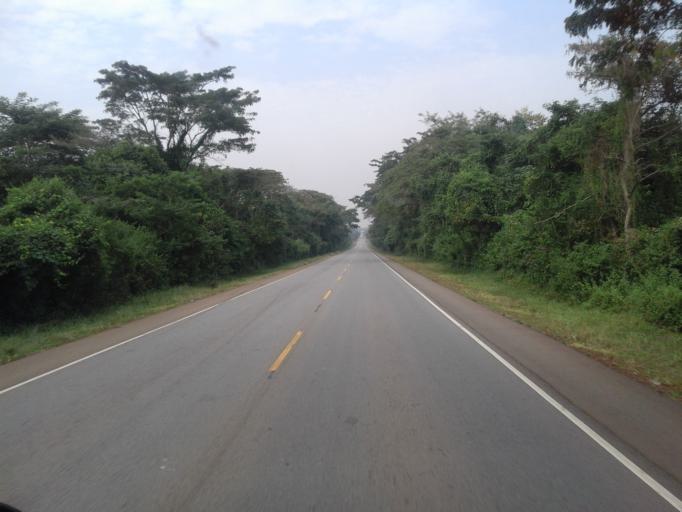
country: UG
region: Eastern Region
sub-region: Busia District
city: Busia
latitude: 0.5301
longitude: 33.9821
